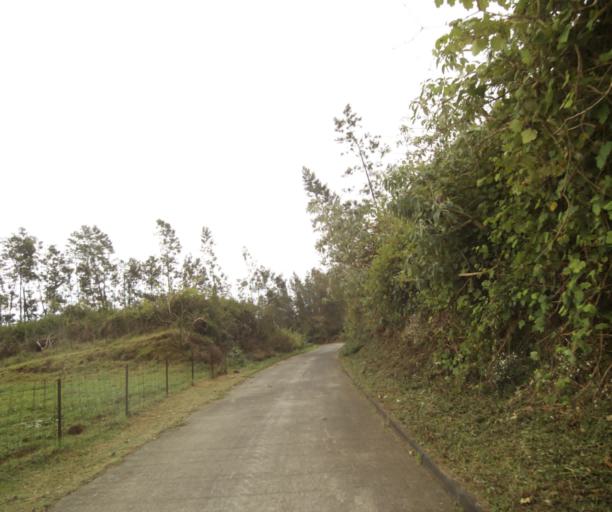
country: RE
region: Reunion
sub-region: Reunion
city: Saint-Paul
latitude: -21.0177
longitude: 55.3532
